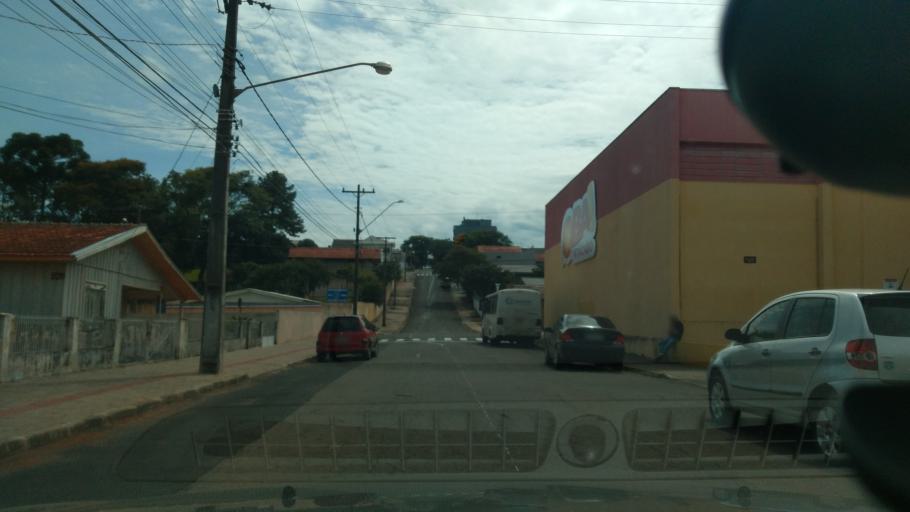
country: BR
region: Parana
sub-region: Guarapuava
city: Guarapuava
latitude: -25.3898
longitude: -51.4699
